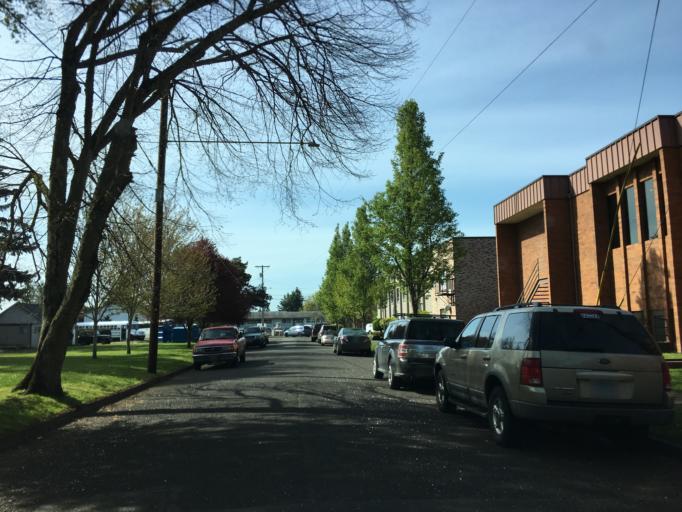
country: US
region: Oregon
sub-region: Multnomah County
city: Lents
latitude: 45.5246
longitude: -122.5694
